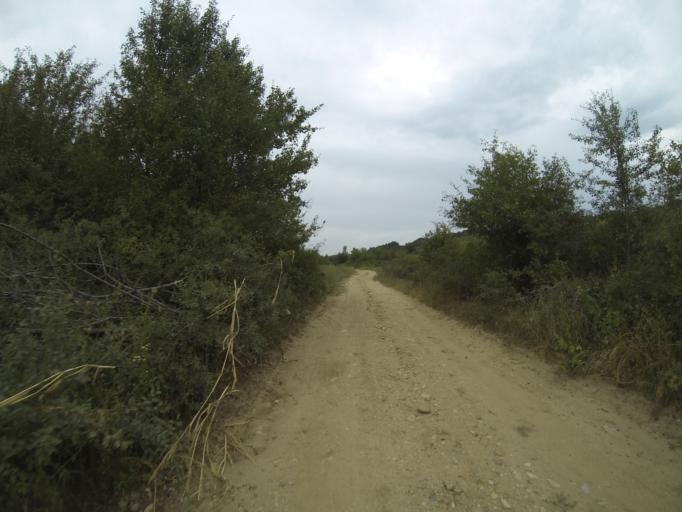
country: RO
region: Dolj
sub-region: Comuna Bradesti
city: Bradesti
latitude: 44.5144
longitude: 23.6368
